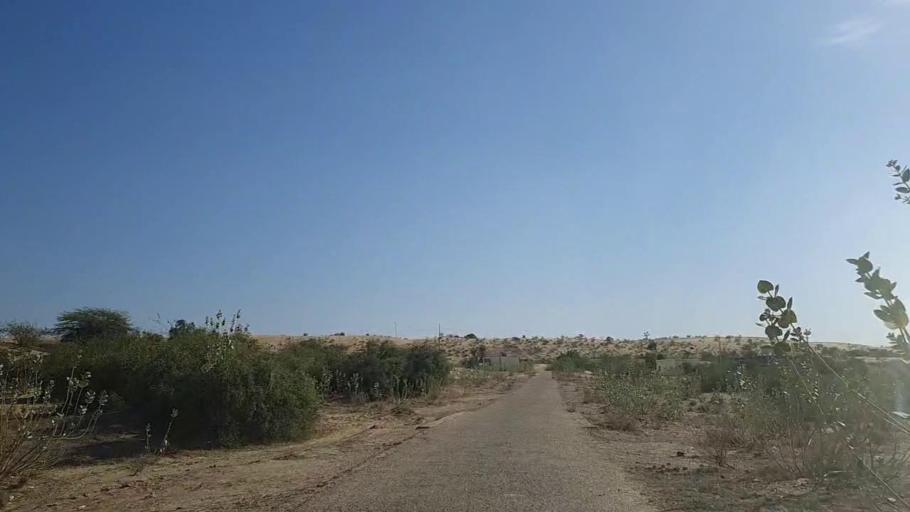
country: PK
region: Sindh
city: Naukot
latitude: 24.8353
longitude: 69.5542
